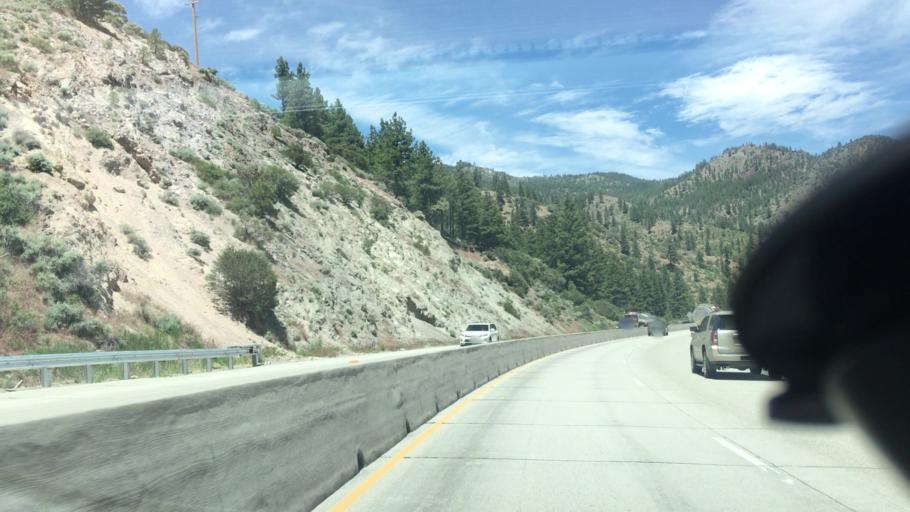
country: US
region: Nevada
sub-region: Washoe County
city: Verdi
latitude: 39.4241
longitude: -120.0359
